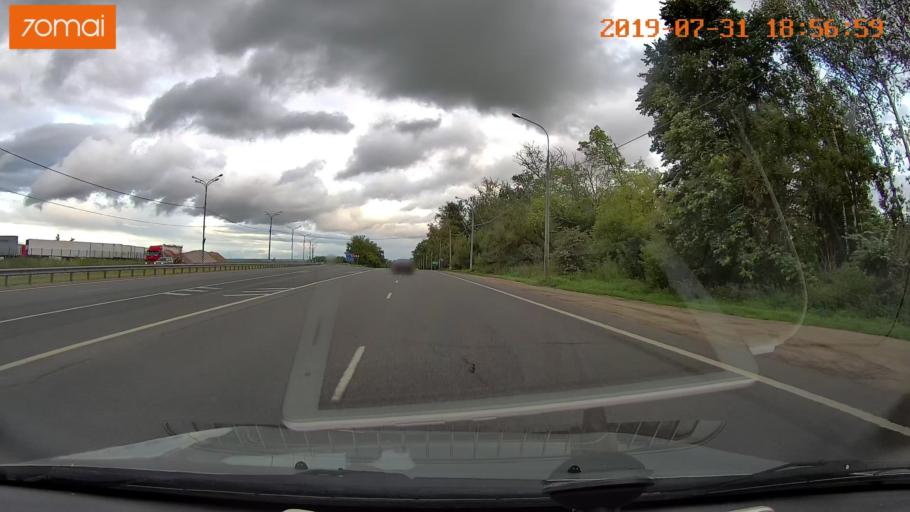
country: RU
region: Moskovskaya
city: Raduzhnyy
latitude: 55.1580
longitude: 38.6858
